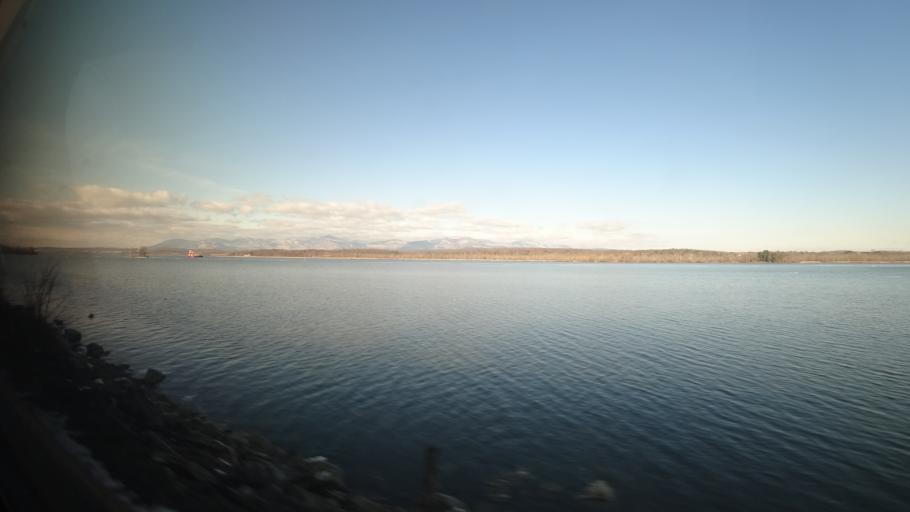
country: US
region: New York
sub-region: Greene County
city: Catskill
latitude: 42.1875
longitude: -73.8530
